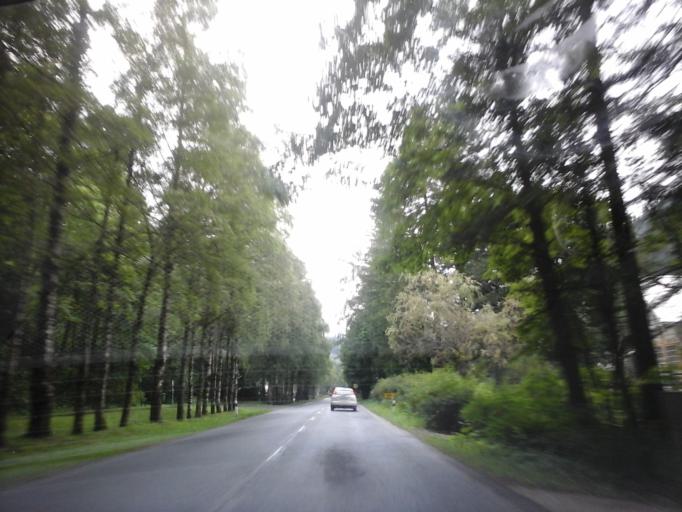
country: SK
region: Presovsky
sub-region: Okres Poprad
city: Zdiar
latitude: 49.2265
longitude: 20.3219
